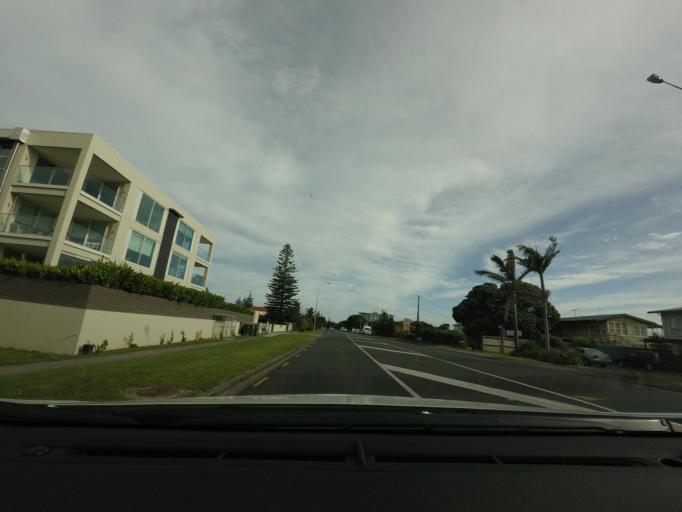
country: NZ
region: Auckland
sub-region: Auckland
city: Rothesay Bay
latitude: -36.5814
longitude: 174.6933
